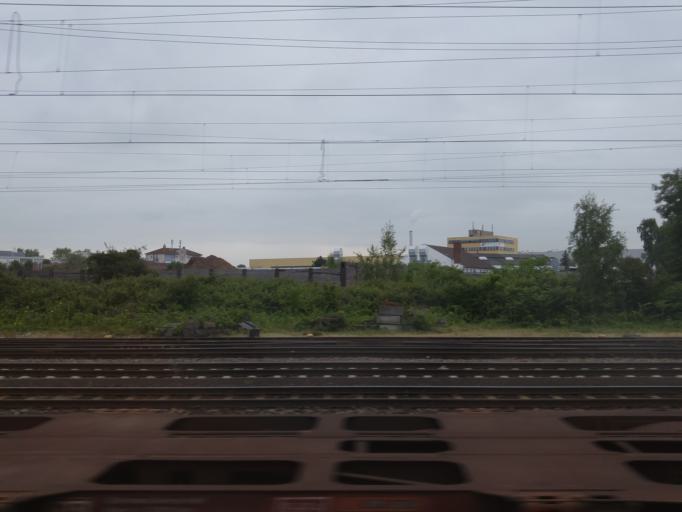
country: DE
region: Hesse
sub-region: Regierungsbezirk Darmstadt
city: Darmstadt
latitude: 49.8816
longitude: 8.6276
